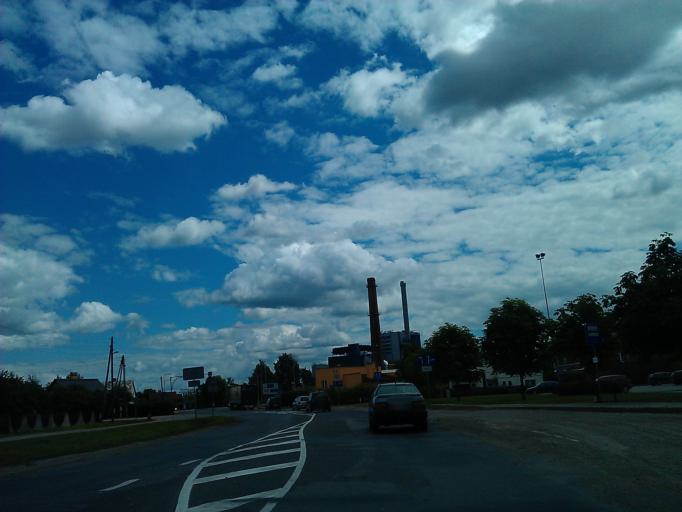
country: LV
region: Jelgava
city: Jelgava
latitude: 56.6373
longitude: 23.7052
